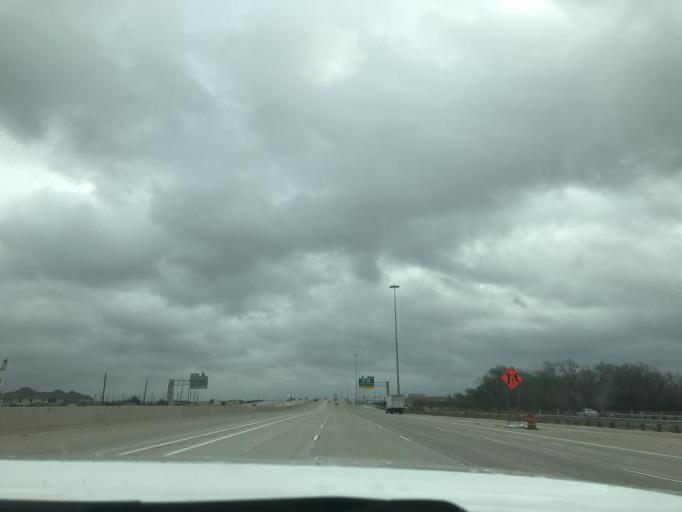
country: US
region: Texas
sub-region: Fort Bend County
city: Richmond
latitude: 29.5547
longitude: -95.7228
